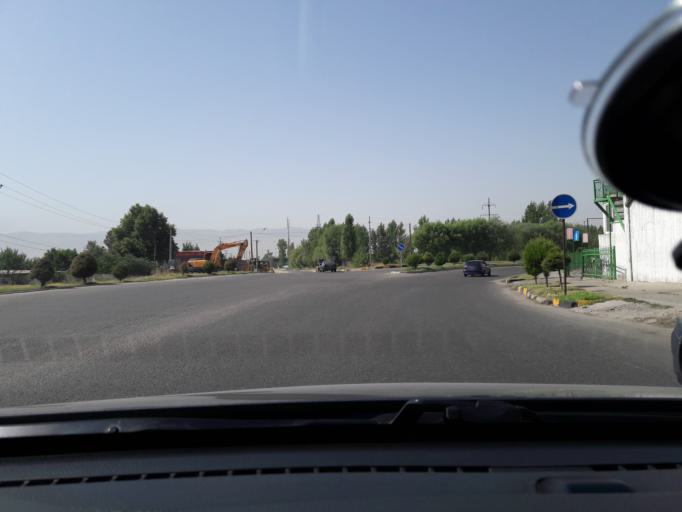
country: TJ
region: Dushanbe
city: Dushanbe
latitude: 38.5018
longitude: 68.7601
